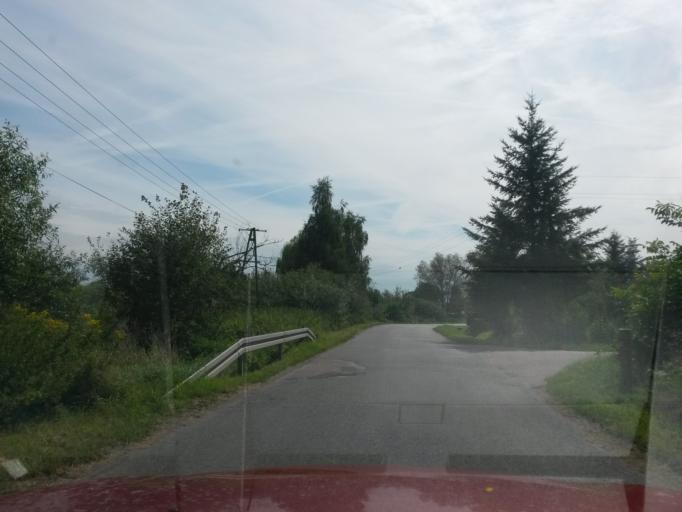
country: PL
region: Lesser Poland Voivodeship
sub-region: Powiat wielicki
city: Szarow
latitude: 49.9878
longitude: 20.2739
